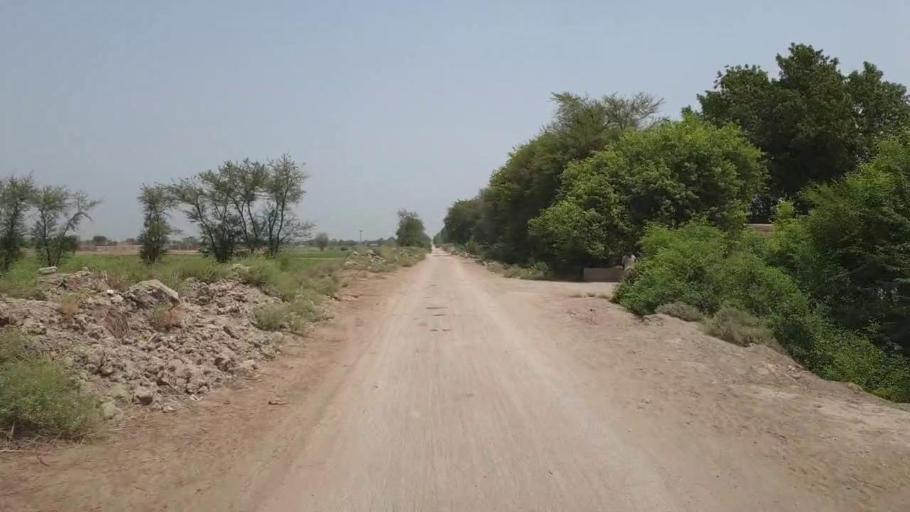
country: PK
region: Sindh
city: Nawabshah
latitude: 26.3085
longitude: 68.3022
